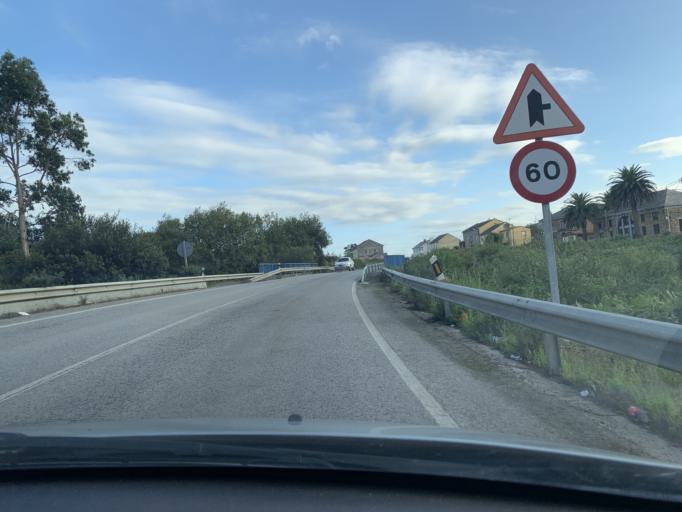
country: ES
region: Galicia
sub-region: Provincia de Lugo
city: Foz
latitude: 43.5596
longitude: -7.2704
